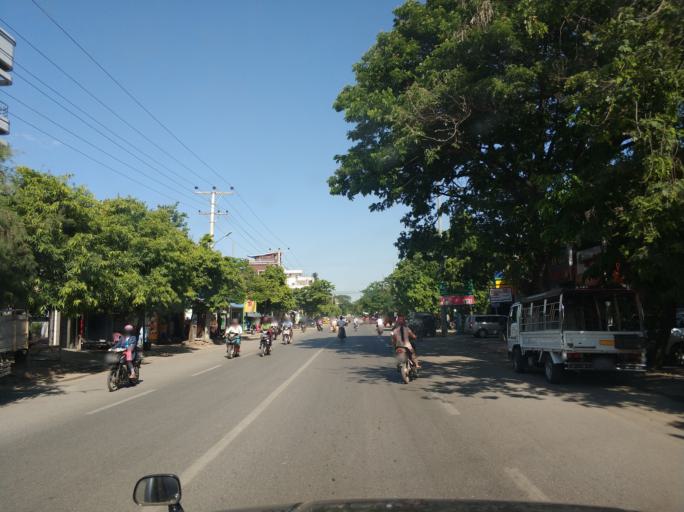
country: MM
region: Mandalay
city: Mandalay
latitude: 21.9704
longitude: 96.0677
